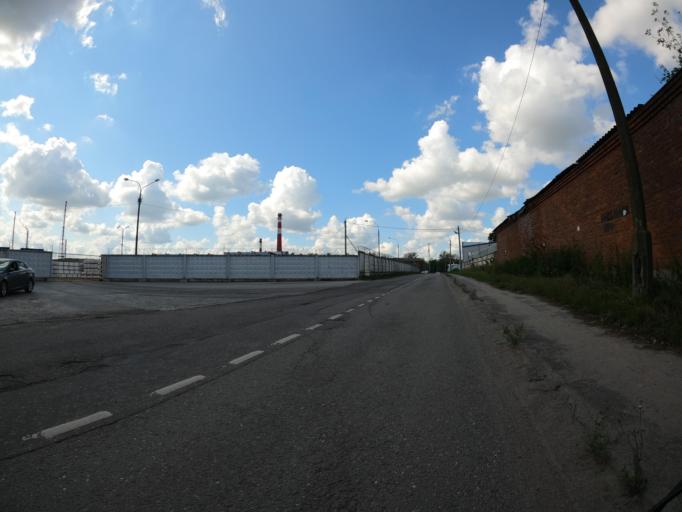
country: RU
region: Moskovskaya
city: Voskresensk
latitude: 55.3132
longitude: 38.6934
